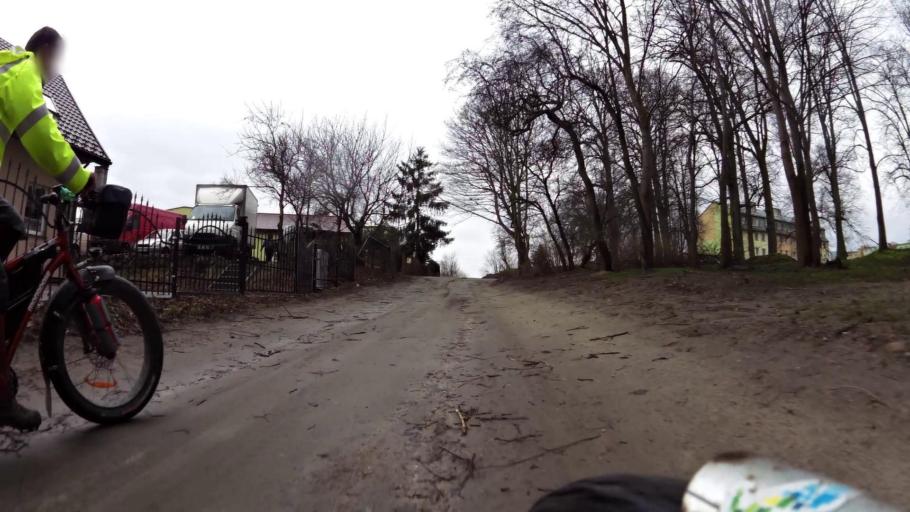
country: PL
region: Pomeranian Voivodeship
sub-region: Powiat bytowski
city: Miastko
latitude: 54.0066
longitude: 16.9856
